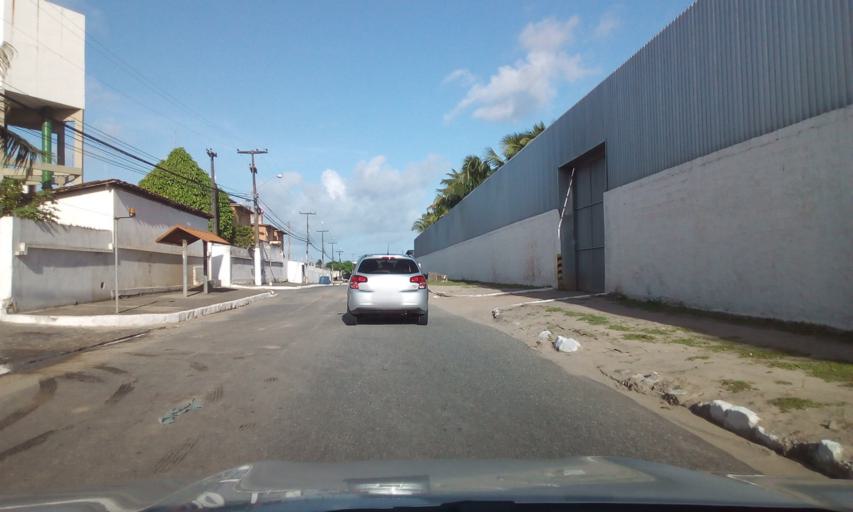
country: BR
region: Paraiba
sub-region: Joao Pessoa
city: Joao Pessoa
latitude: -7.1646
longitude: -34.8599
